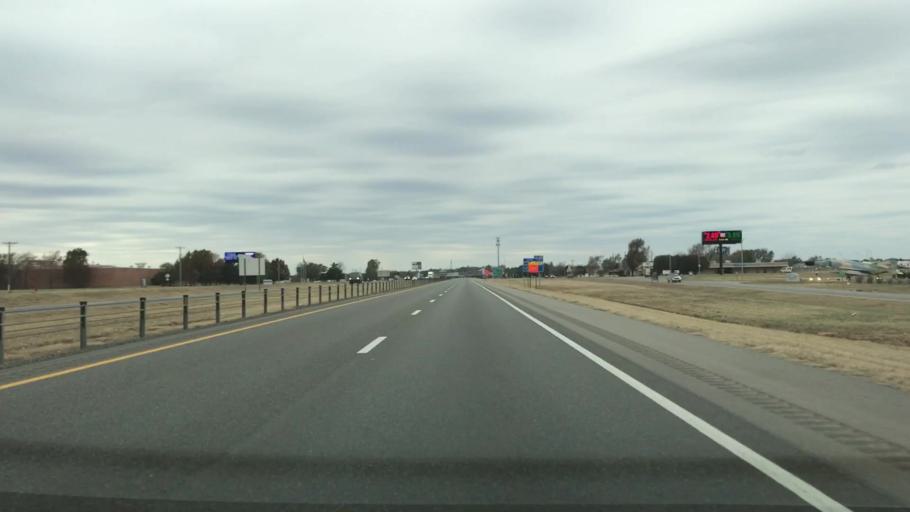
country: US
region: Oklahoma
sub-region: Custer County
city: Weatherford
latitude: 35.5364
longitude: -98.6682
